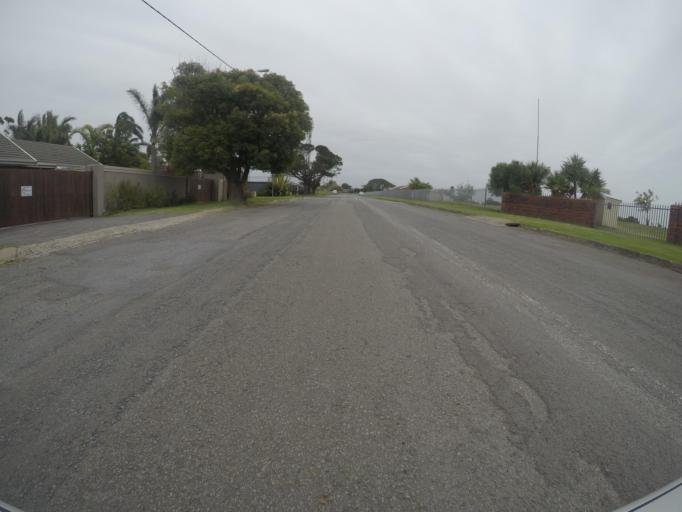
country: ZA
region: Eastern Cape
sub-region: Buffalo City Metropolitan Municipality
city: East London
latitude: -32.9682
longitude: 27.9347
